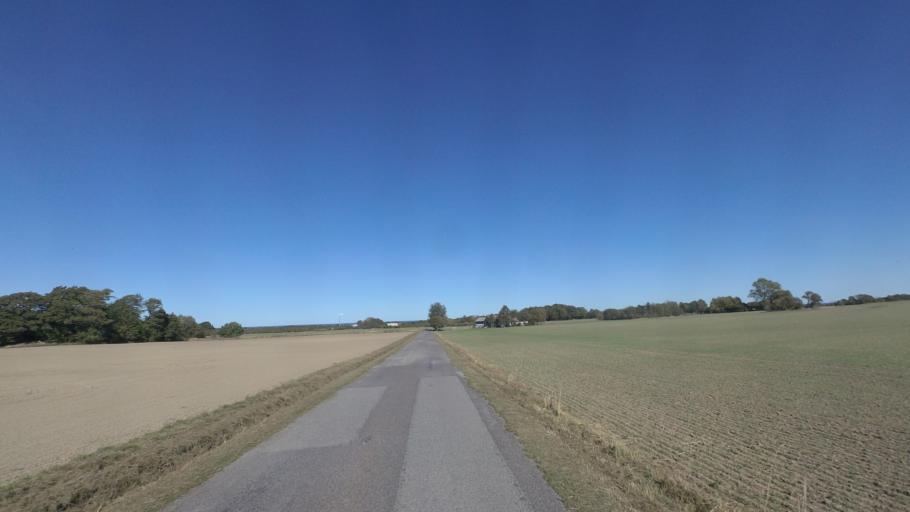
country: DK
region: Capital Region
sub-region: Bornholm Kommune
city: Nexo
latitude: 55.1190
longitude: 15.0467
